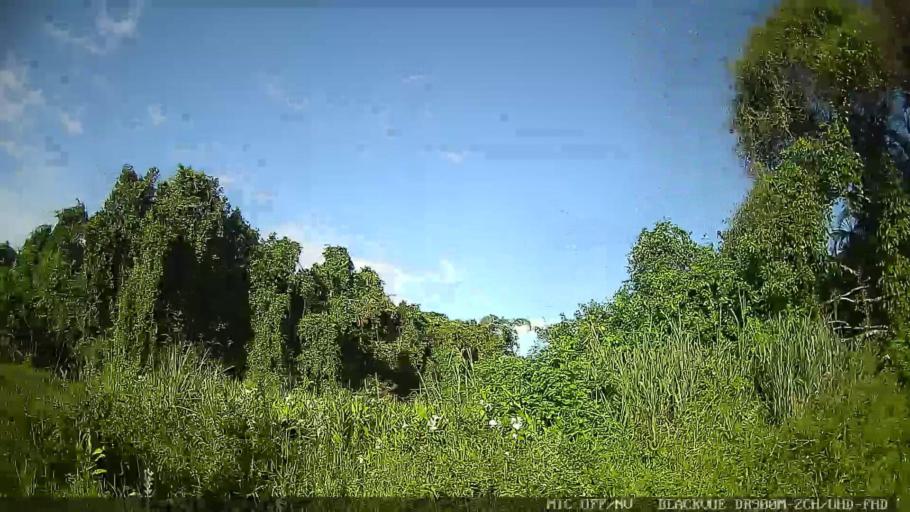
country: BR
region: Sao Paulo
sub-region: Itanhaem
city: Itanhaem
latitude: -24.2133
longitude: -46.8708
